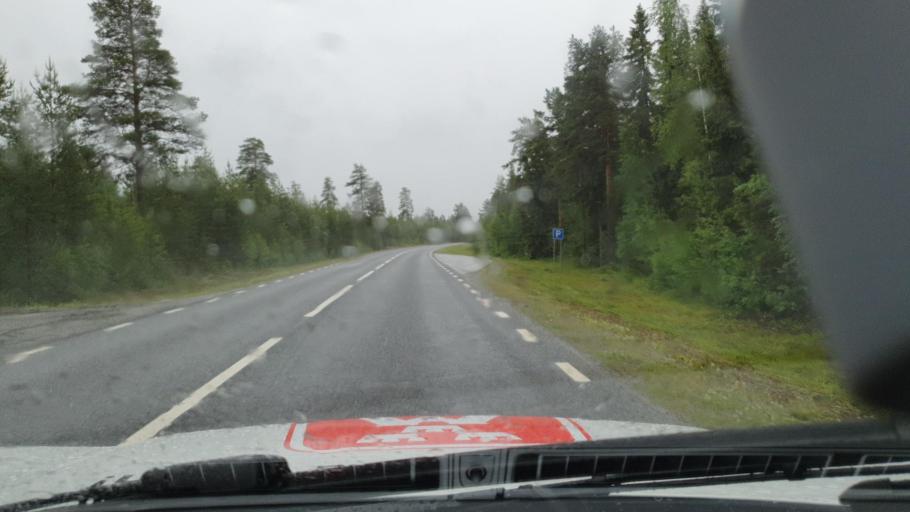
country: SE
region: Vaesterbotten
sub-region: Asele Kommun
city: Asele
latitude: 64.1160
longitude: 17.3291
